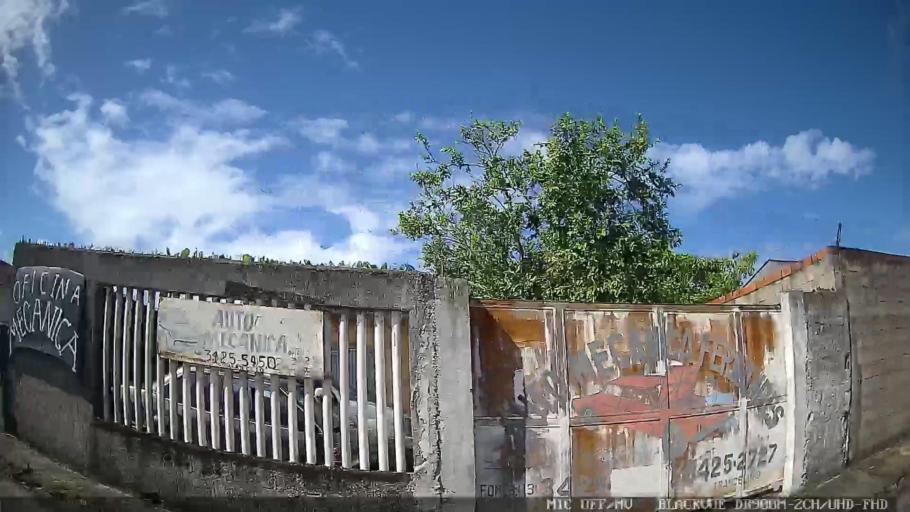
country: BR
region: Sao Paulo
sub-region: Itanhaem
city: Itanhaem
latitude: -24.2235
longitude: -46.8632
